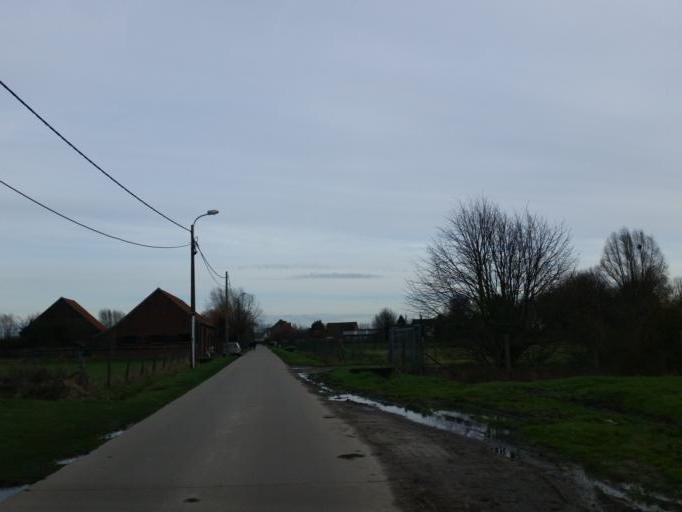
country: BE
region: Flanders
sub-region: Provincie Vlaams-Brabant
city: Kapelle-op-den-Bos
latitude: 51.0043
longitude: 4.4126
